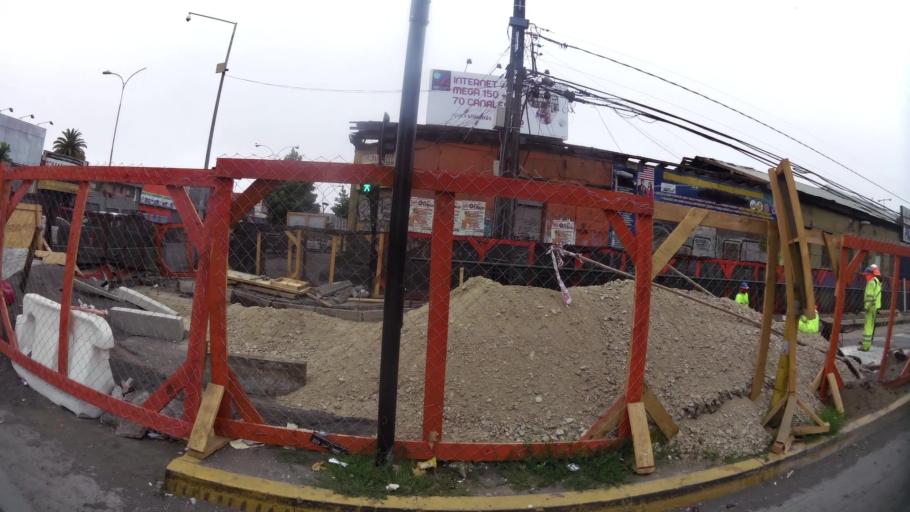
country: CL
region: Biobio
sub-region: Provincia de Concepcion
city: Concepcion
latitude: -36.8271
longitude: -73.0607
